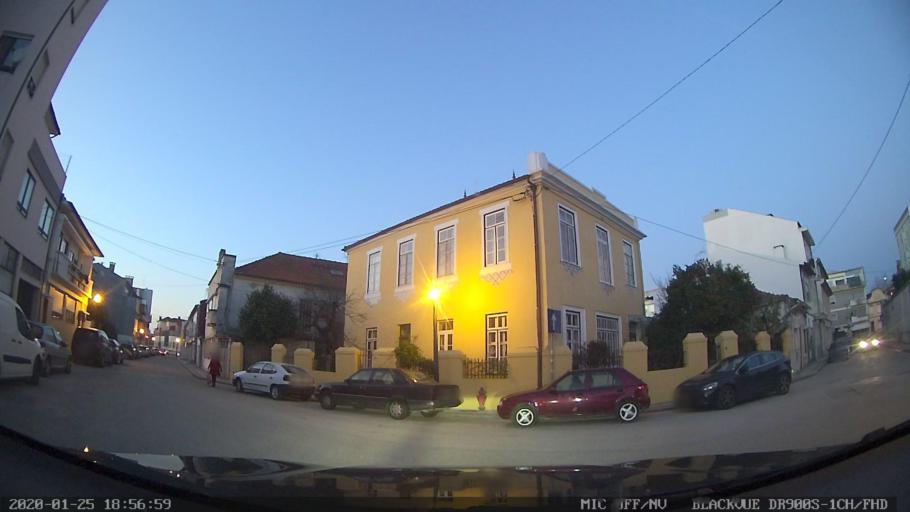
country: PT
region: Aveiro
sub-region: Aveiro
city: Aveiro
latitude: 40.6371
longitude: -8.6511
